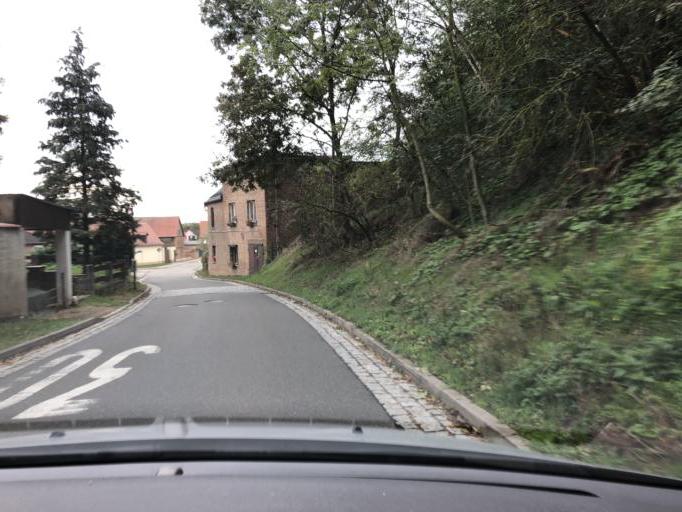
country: DE
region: Saxony-Anhalt
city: Uichteritz
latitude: 51.2167
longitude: 11.9401
